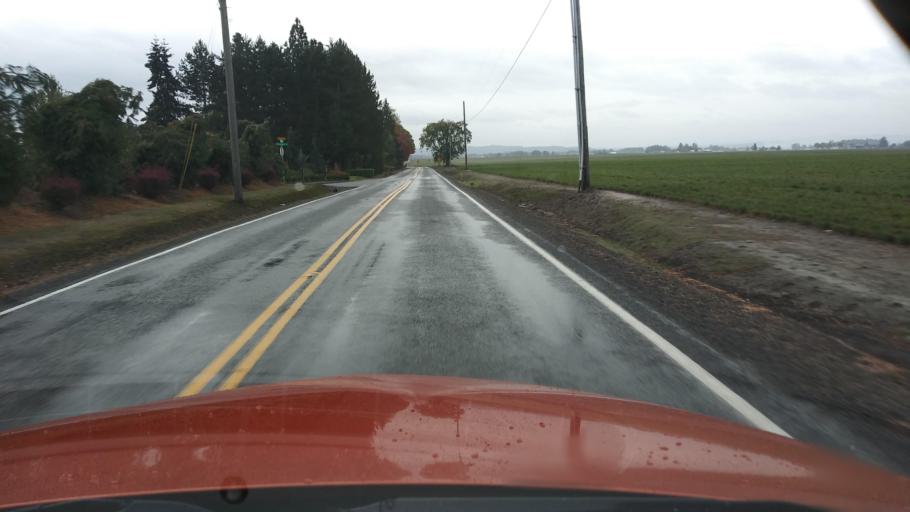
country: US
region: Oregon
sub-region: Washington County
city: North Plains
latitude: 45.5949
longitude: -123.0145
